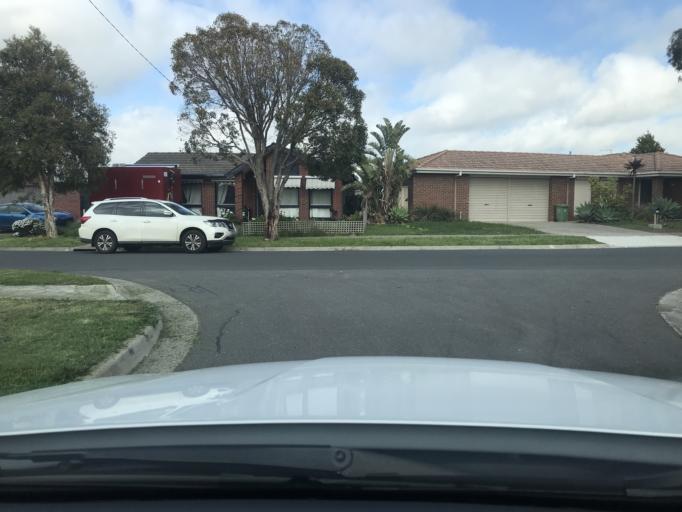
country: AU
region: Victoria
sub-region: Hume
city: Craigieburn
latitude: -37.6055
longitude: 144.9315
